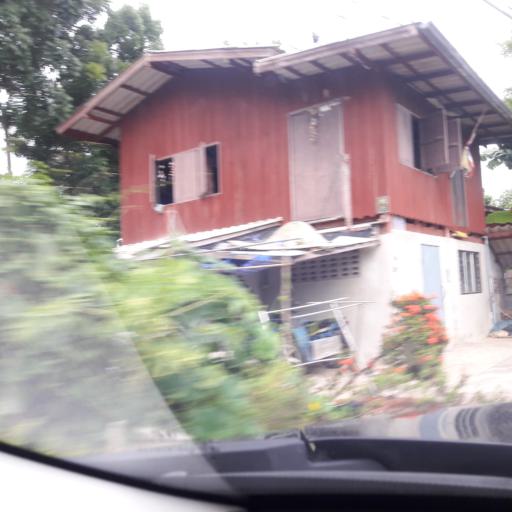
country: TH
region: Ratchaburi
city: Damnoen Saduak
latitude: 13.5620
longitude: 99.9462
